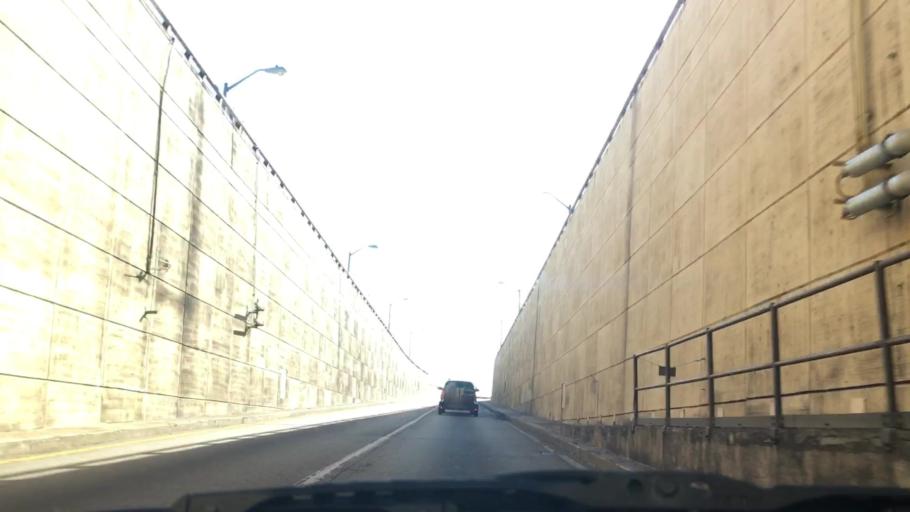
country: US
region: Virginia
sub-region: City of Hampton
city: East Hampton
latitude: 36.9970
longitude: -76.3124
